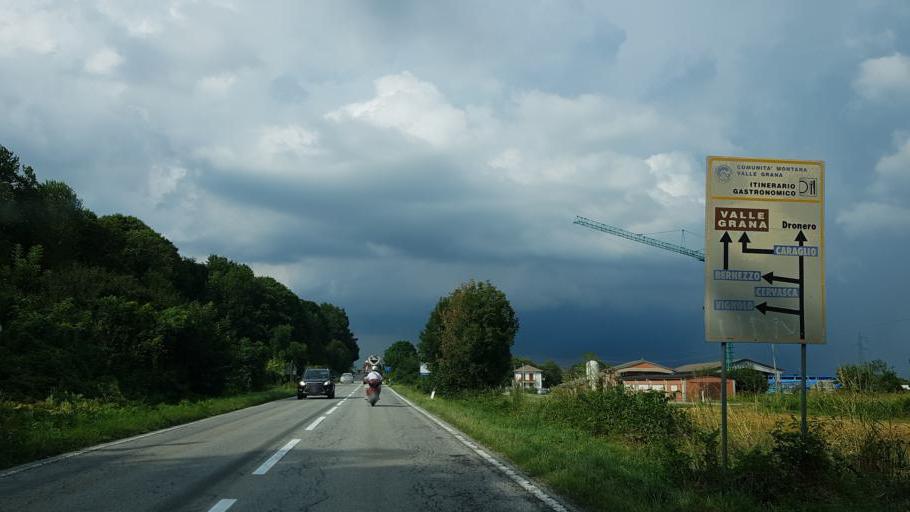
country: IT
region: Piedmont
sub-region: Provincia di Cuneo
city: Vignolo
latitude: 44.3513
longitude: 7.4771
